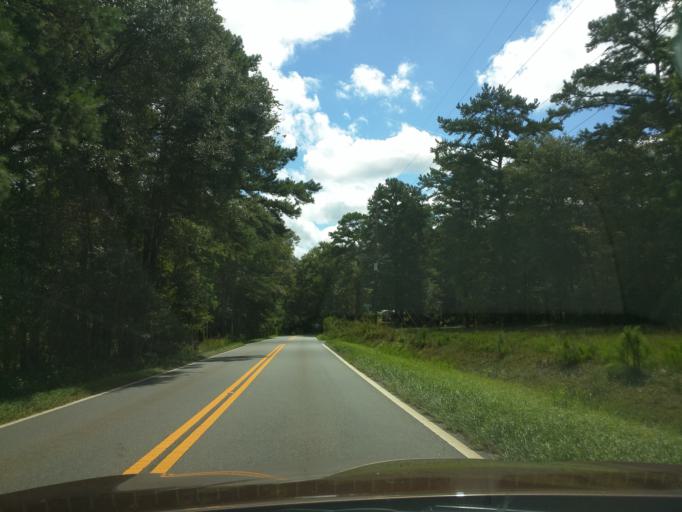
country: US
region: Florida
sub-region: Gadsden County
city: Havana
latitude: 30.5873
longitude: -84.2701
